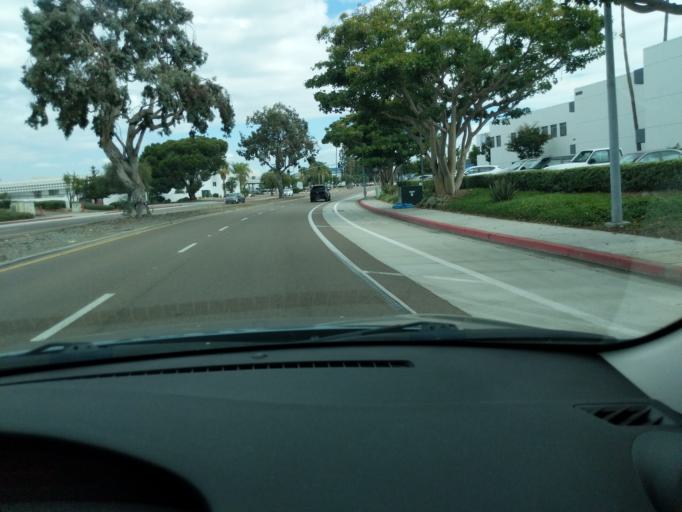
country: US
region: California
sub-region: San Diego County
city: San Diego
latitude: 32.8220
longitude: -117.1339
